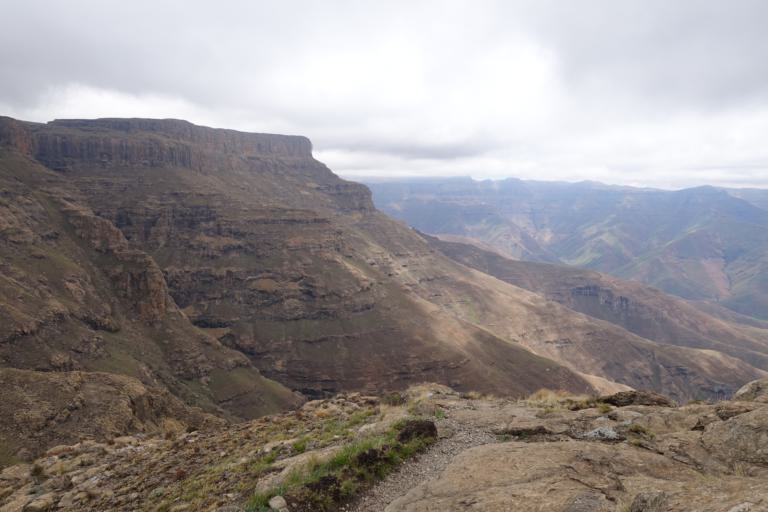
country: ZA
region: Orange Free State
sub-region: Thabo Mofutsanyana District Municipality
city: Phuthaditjhaba
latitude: -28.7400
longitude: 28.8866
